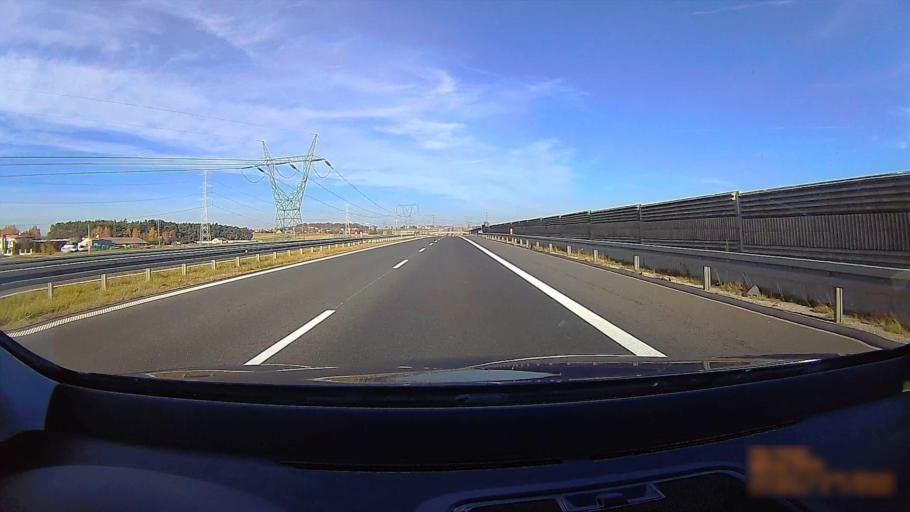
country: PL
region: Greater Poland Voivodeship
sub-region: Powiat ostrowski
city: Przygodzice
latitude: 51.6047
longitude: 17.8543
